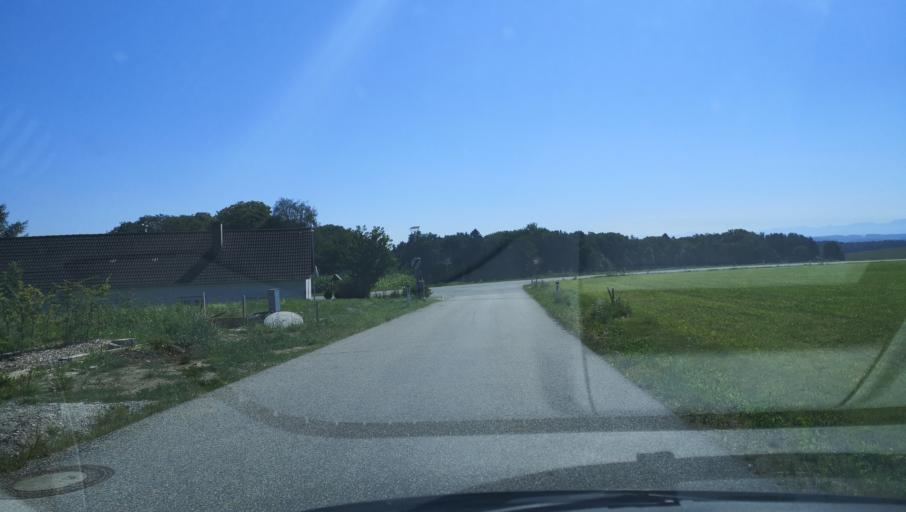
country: AT
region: Lower Austria
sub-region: Politischer Bezirk Melk
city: Neumarkt an der Ybbs
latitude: 48.1613
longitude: 15.0222
